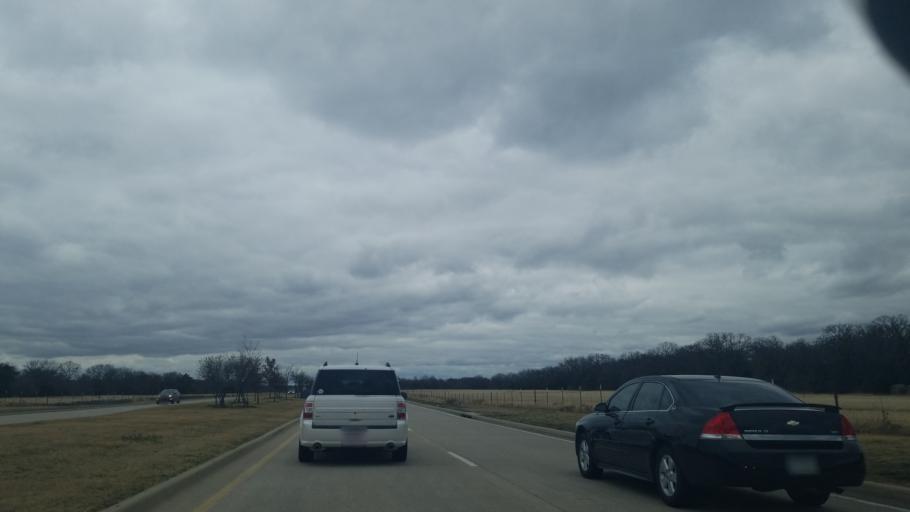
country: US
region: Texas
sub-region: Denton County
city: Copper Canyon
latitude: 33.1111
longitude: -97.0788
